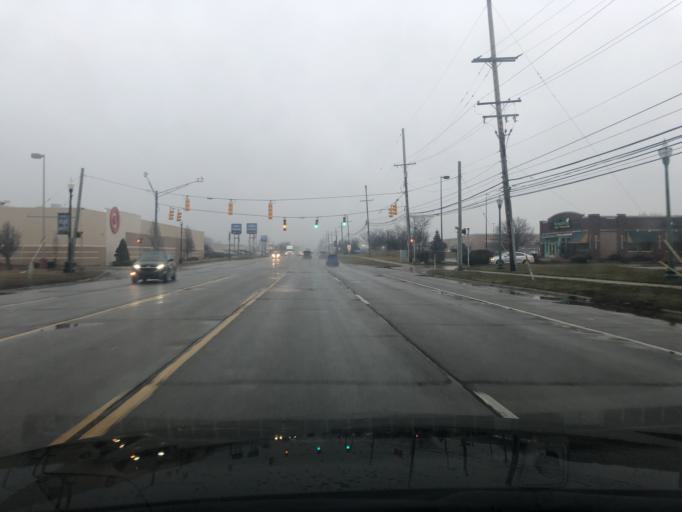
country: US
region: Michigan
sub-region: Wayne County
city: Woodhaven
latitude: 42.1384
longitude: -83.2261
